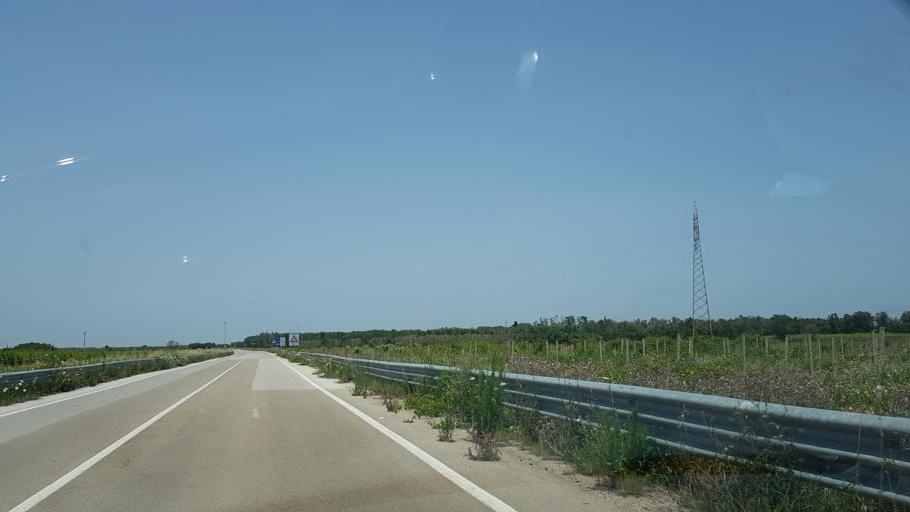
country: IT
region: Apulia
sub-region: Provincia di Brindisi
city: San Pancrazio Salentino
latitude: 40.4809
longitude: 17.8358
